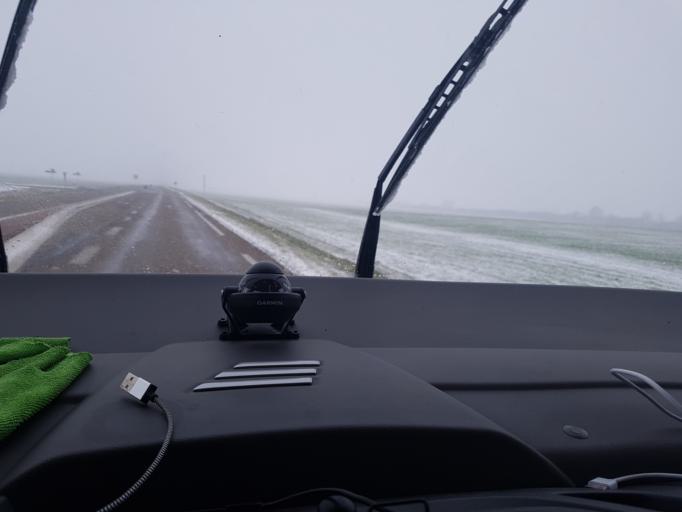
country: FR
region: Lorraine
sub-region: Departement de la Moselle
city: Chateau-Salins
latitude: 48.8751
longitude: 6.4139
